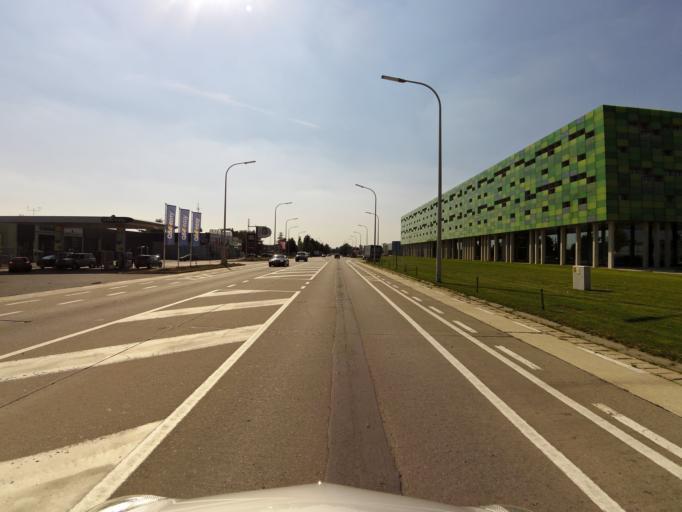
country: BE
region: Flanders
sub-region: Provincie West-Vlaanderen
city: Torhout
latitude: 51.0750
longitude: 3.1069
